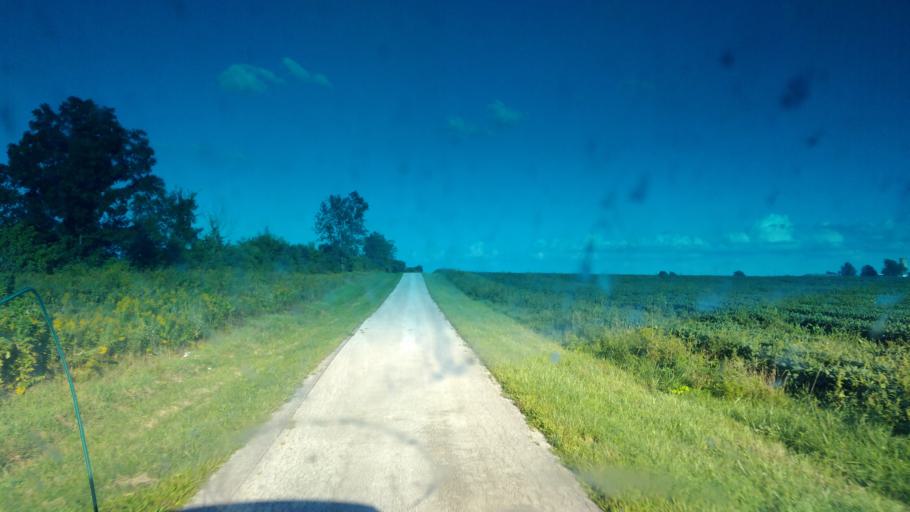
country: US
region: Ohio
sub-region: Wyandot County
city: Carey
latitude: 40.9413
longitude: -83.4358
